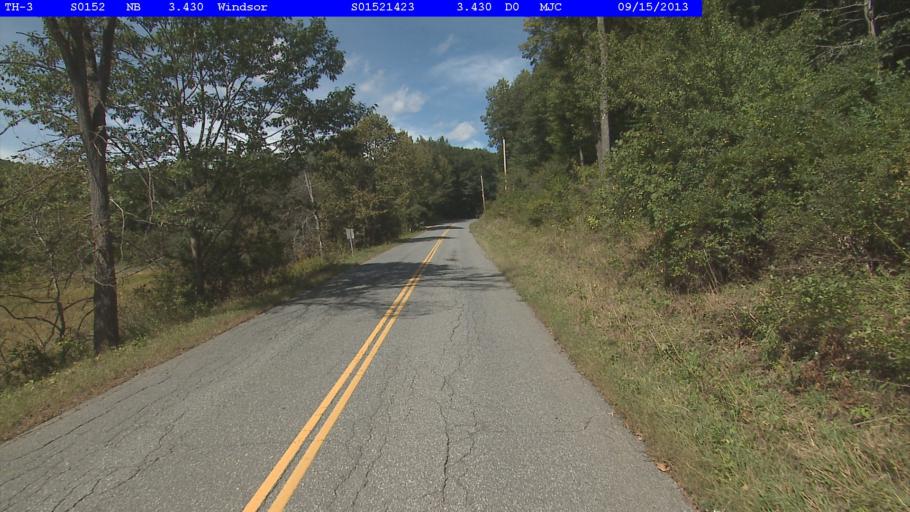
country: US
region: Vermont
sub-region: Windsor County
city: Windsor
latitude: 43.5102
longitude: -72.4336
